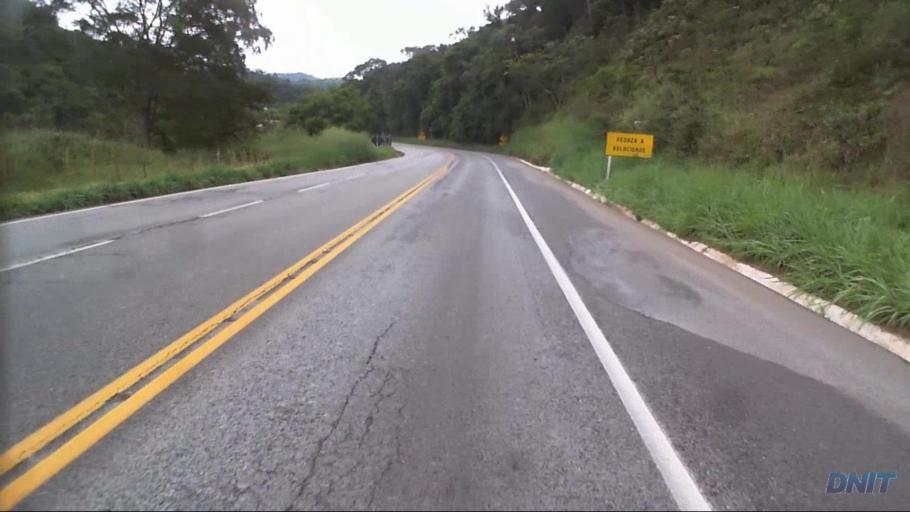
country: BR
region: Minas Gerais
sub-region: Joao Monlevade
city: Joao Monlevade
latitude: -19.8377
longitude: -43.3431
